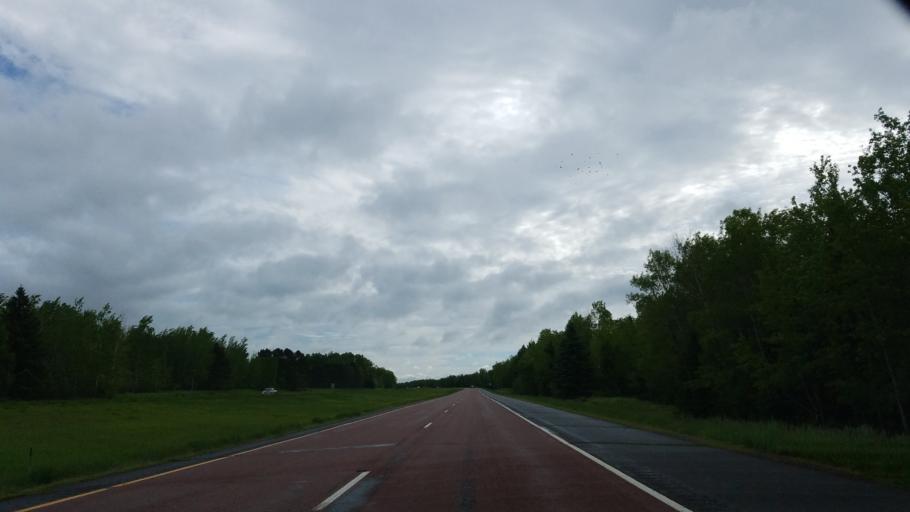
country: US
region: Minnesota
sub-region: Saint Louis County
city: Arnold
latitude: 46.8916
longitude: -91.9157
